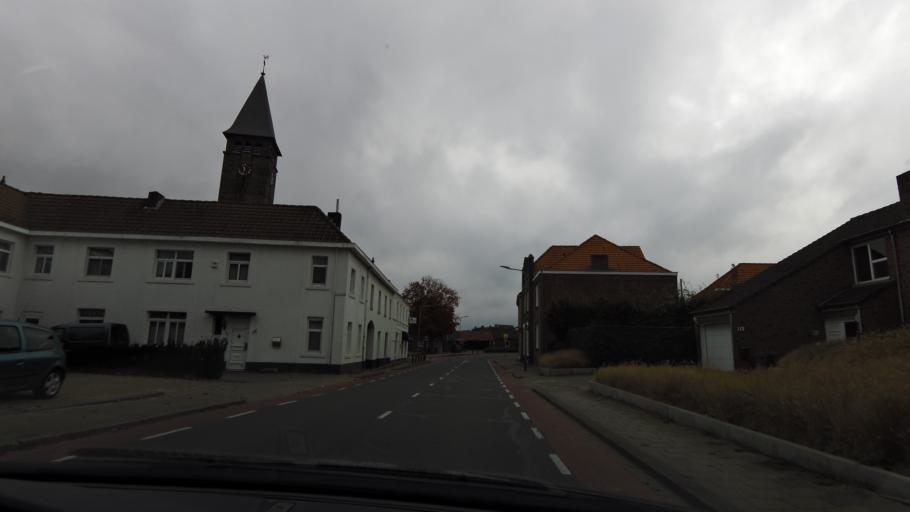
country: NL
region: Limburg
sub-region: Gemeente Schinnen
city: Puth
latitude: 50.9562
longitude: 5.8695
